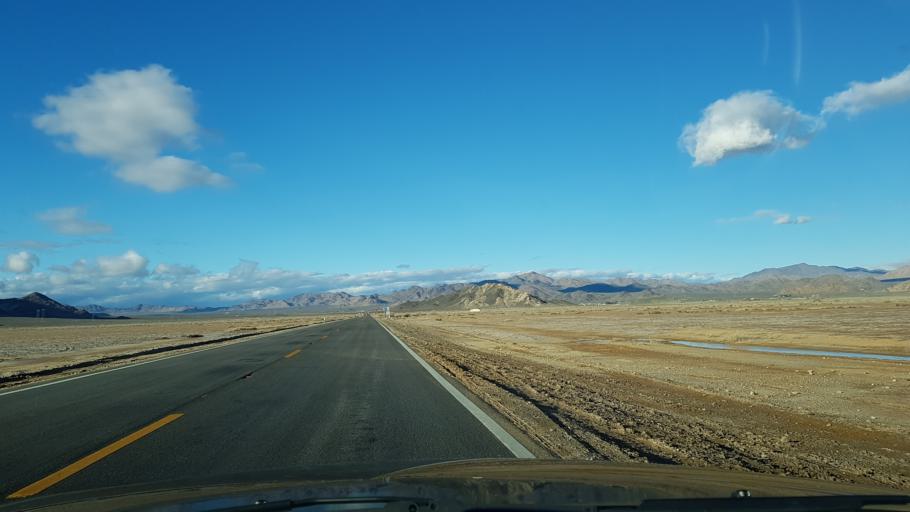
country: US
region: California
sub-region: San Bernardino County
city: Lucerne Valley
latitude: 34.5132
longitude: -116.9453
